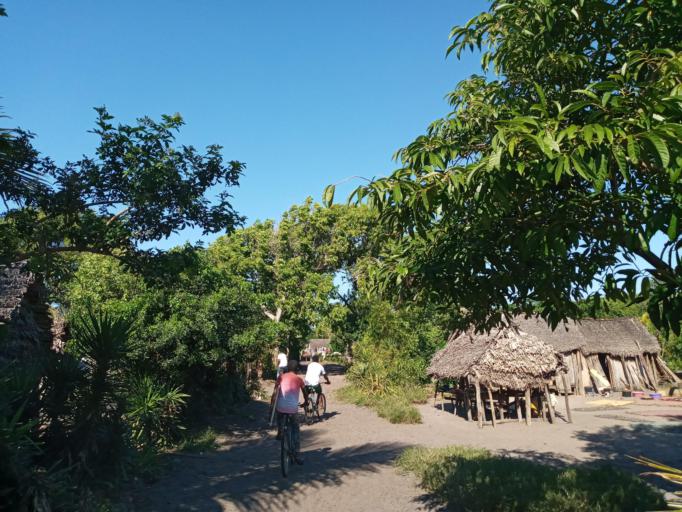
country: MG
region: Anosy
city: Fort Dauphin
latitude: -24.9085
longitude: 47.1044
